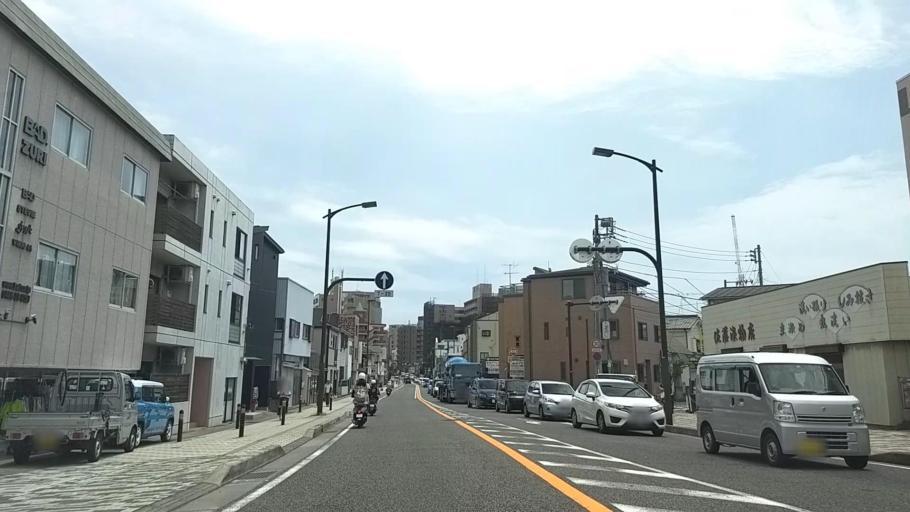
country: JP
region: Kanagawa
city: Fujisawa
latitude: 35.3450
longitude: 139.4871
